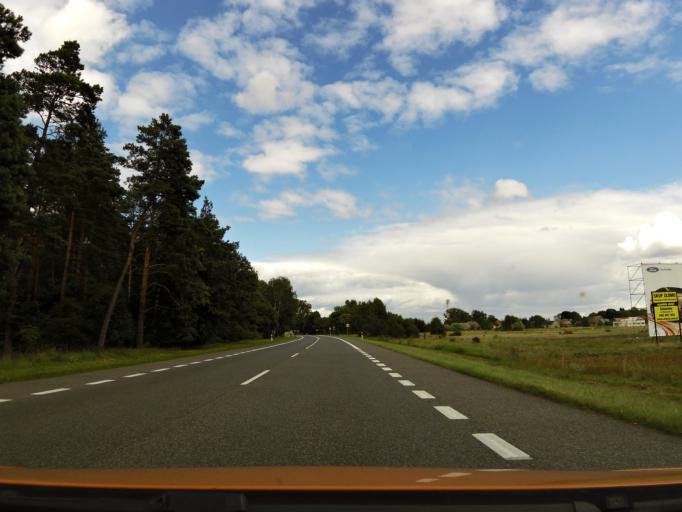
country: PL
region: West Pomeranian Voivodeship
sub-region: Powiat goleniowski
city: Mosty
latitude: 53.6071
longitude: 14.9024
